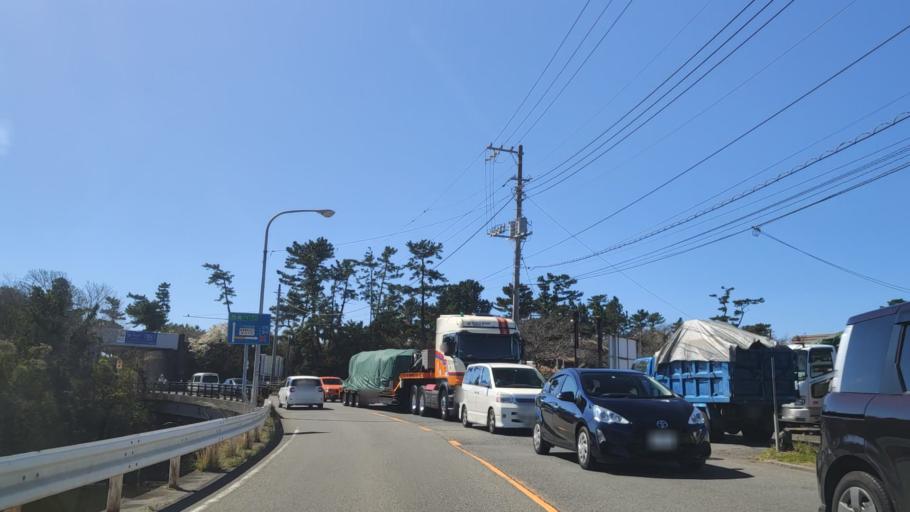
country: JP
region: Kanagawa
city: Oiso
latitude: 35.3032
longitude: 139.2864
